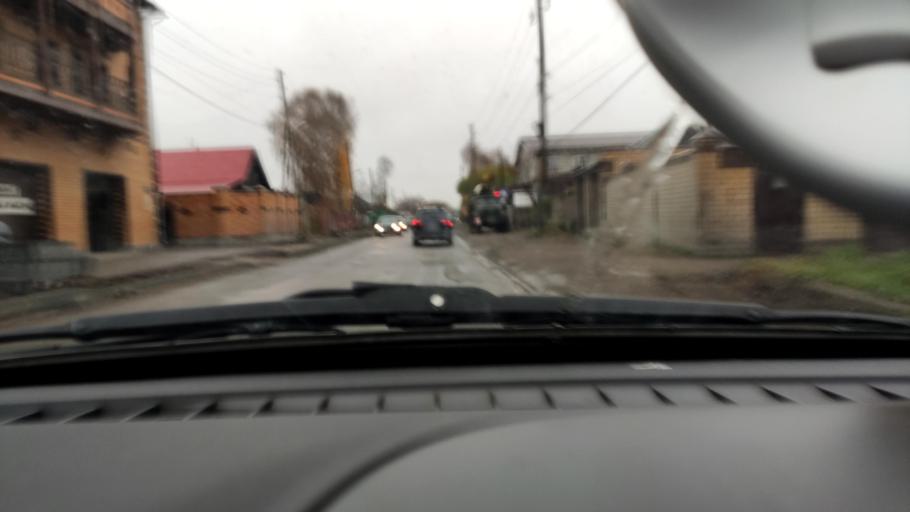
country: RU
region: Perm
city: Kondratovo
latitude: 57.9655
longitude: 56.1198
